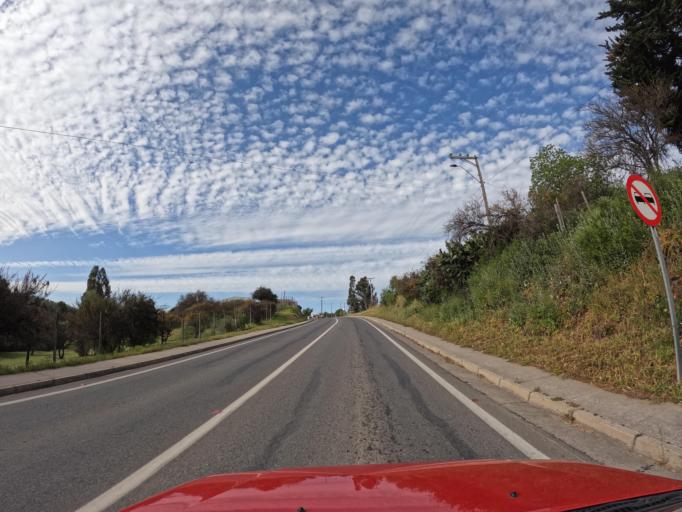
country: CL
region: O'Higgins
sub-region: Provincia de Colchagua
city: Santa Cruz
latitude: -34.2629
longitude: -71.7321
